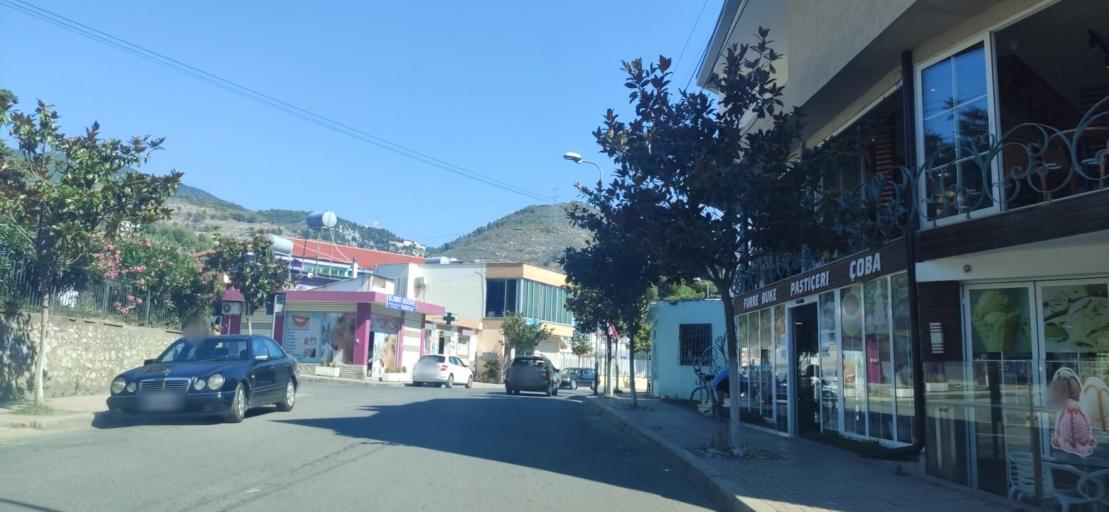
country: AL
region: Lezhe
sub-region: Rrethi i Kurbinit
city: Lac
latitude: 41.6375
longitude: 19.7145
